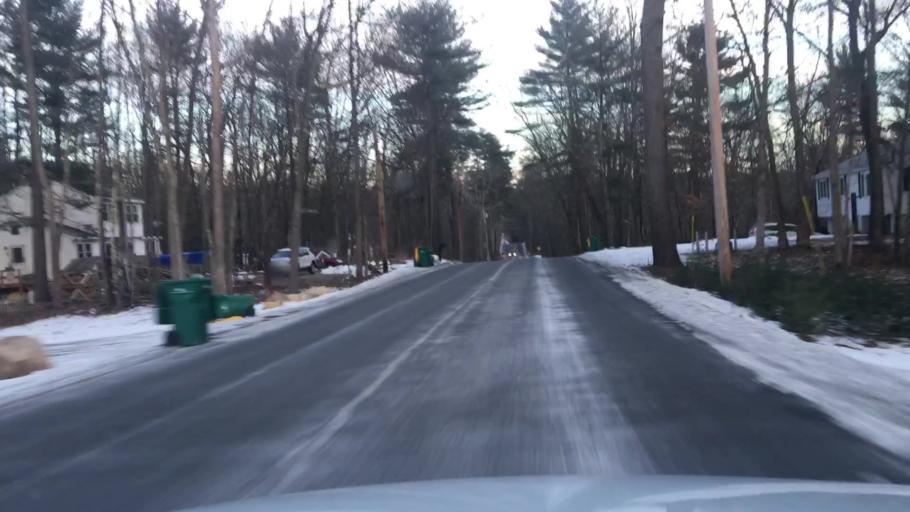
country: US
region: New Hampshire
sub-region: Strafford County
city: Somersworth
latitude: 43.2664
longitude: -70.9253
